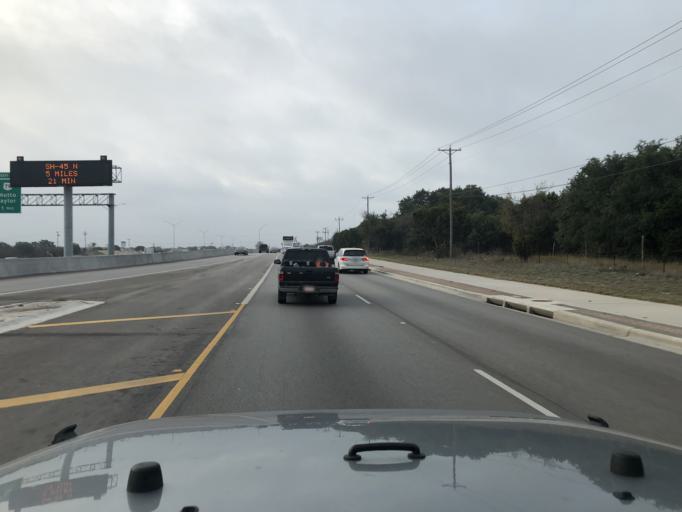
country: US
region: Texas
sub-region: Williamson County
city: Round Rock
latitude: 30.5495
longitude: -97.6929
